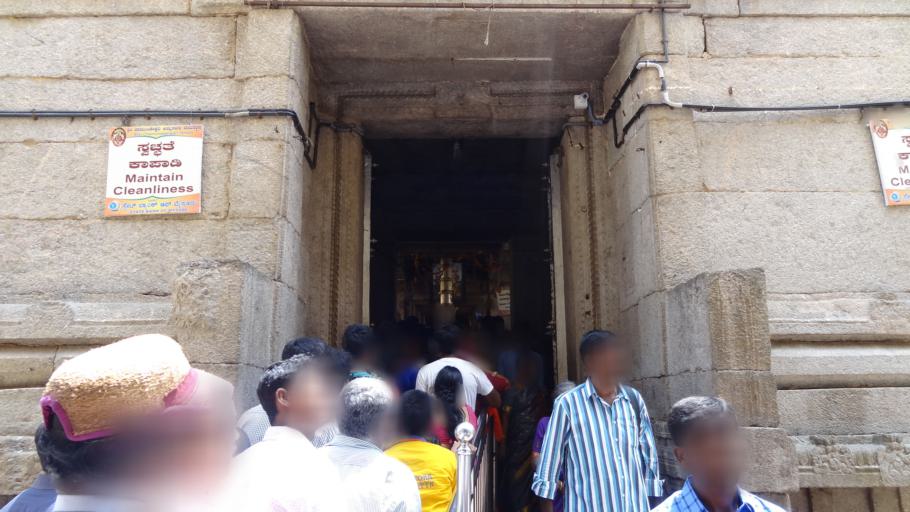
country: IN
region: Karnataka
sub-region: Mysore
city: Mysore
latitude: 12.2724
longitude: 76.6709
